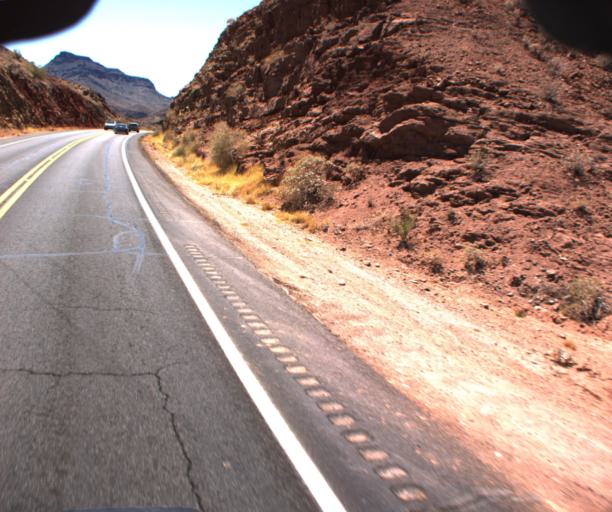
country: US
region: Arizona
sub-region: La Paz County
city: Cienega Springs
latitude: 34.2765
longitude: -114.1306
